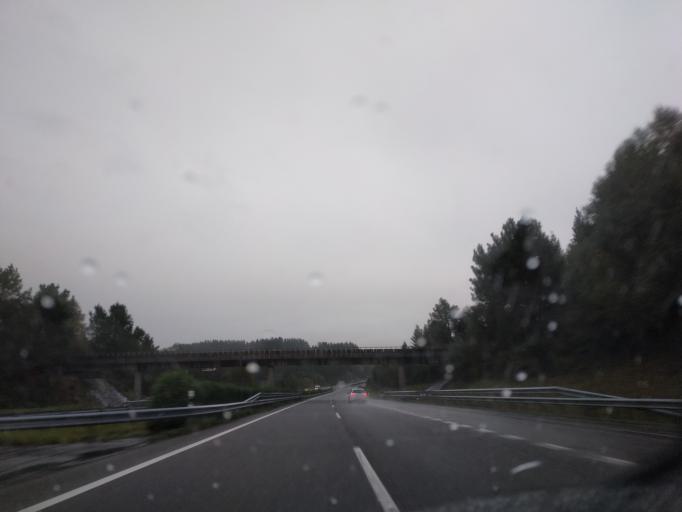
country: ES
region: Galicia
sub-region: Provincia de Lugo
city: Guitiriz
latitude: 43.1828
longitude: -7.8193
